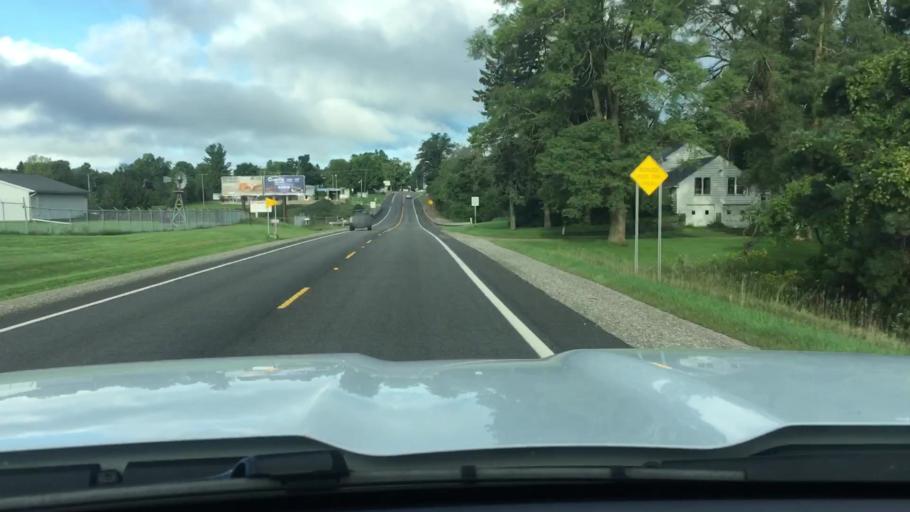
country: US
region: Michigan
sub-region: Lapeer County
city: Barnes Lake-Millers Lake
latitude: 43.3371
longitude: -83.3387
